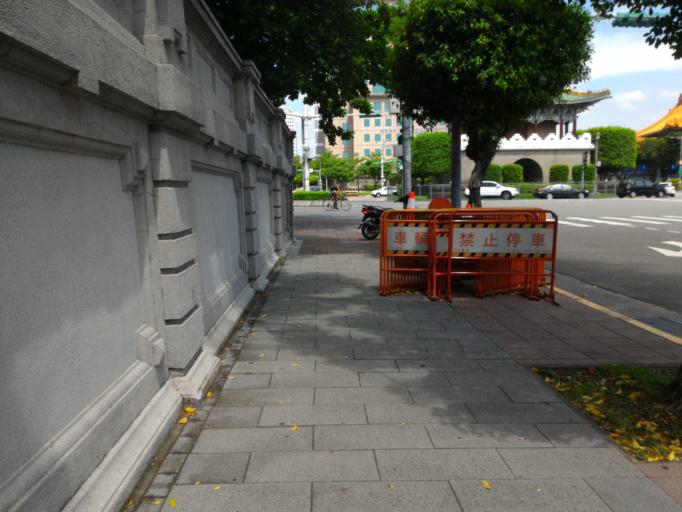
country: TW
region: Taipei
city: Taipei
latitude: 25.0394
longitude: 121.5171
